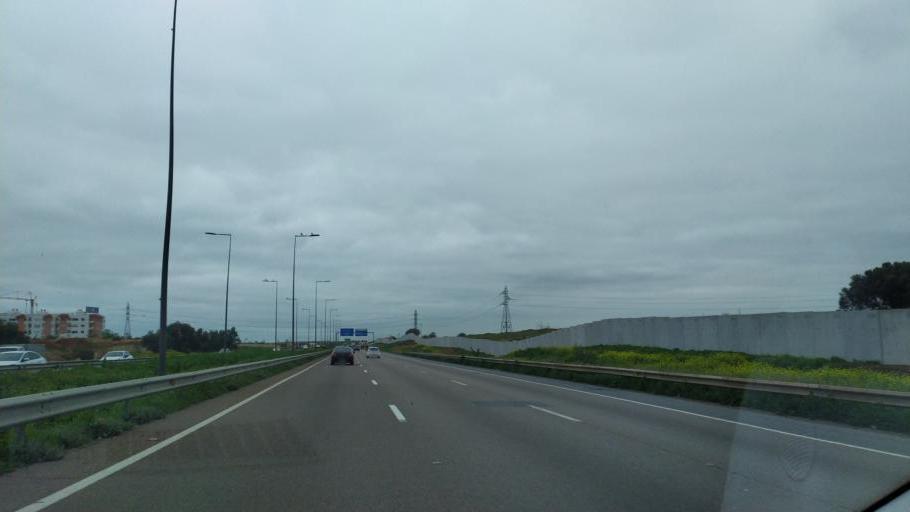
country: MA
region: Grand Casablanca
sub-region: Mohammedia
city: Mohammedia
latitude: 33.6820
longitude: -7.3683
